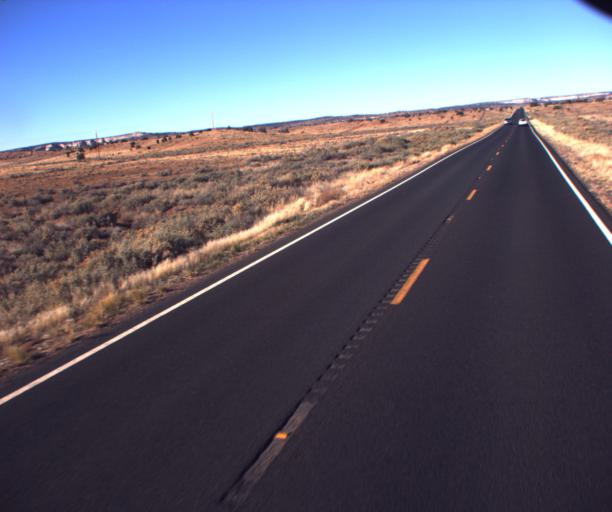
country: US
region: Arizona
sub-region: Apache County
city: Ganado
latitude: 35.7874
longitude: -109.6875
